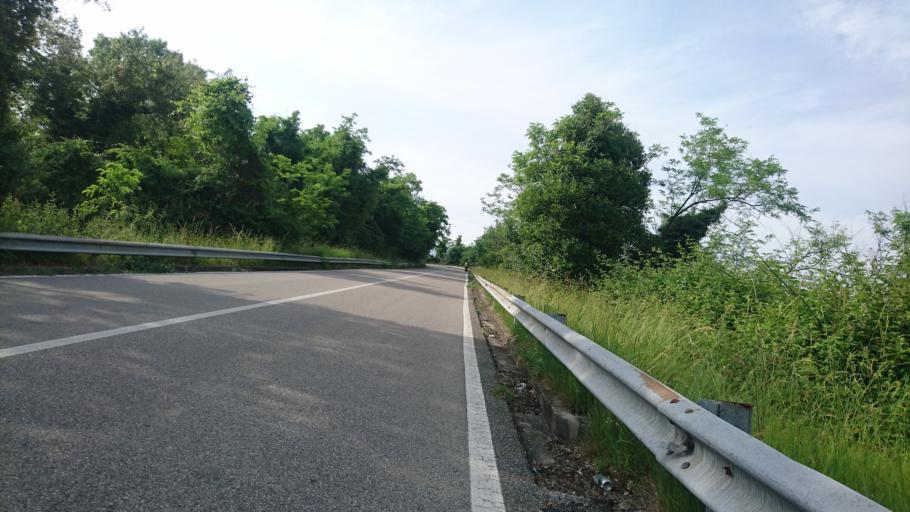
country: IT
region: Veneto
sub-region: Provincia di Treviso
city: Carpesica
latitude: 45.9543
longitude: 12.2938
